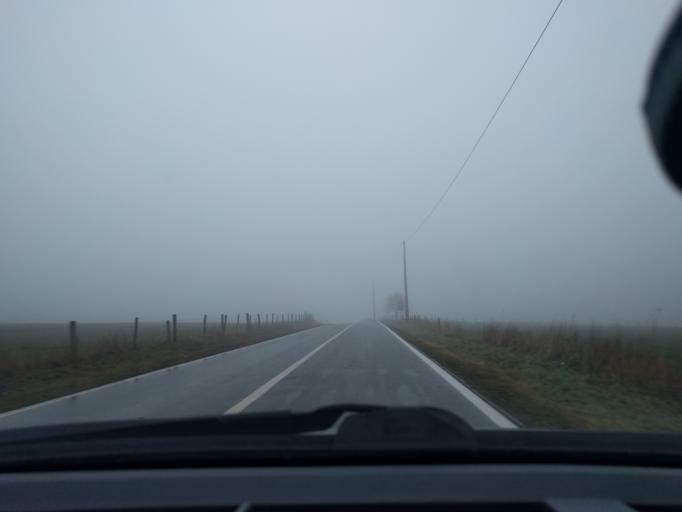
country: BE
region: Wallonia
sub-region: Province du Luxembourg
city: Gouvy
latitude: 50.1999
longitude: 5.9653
